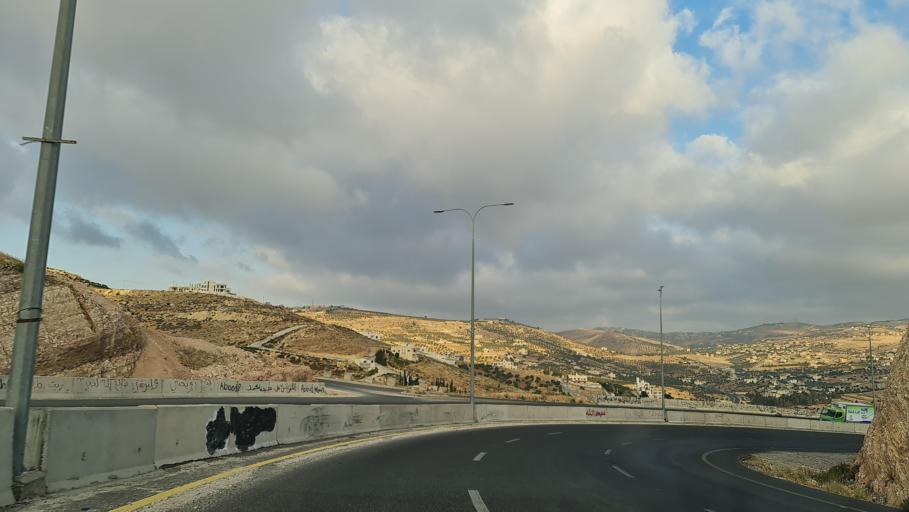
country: JO
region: Zarqa
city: Russeifa
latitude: 32.0910
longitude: 35.9616
